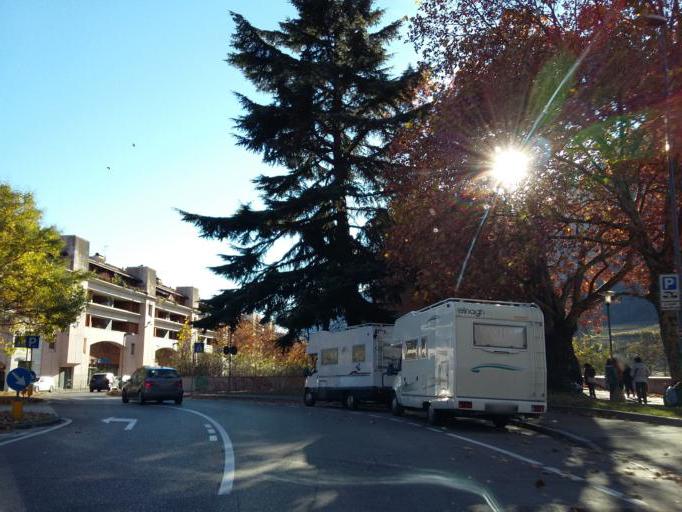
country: IT
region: Trentino-Alto Adige
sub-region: Provincia di Trento
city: Trento
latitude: 46.0684
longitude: 11.1151
